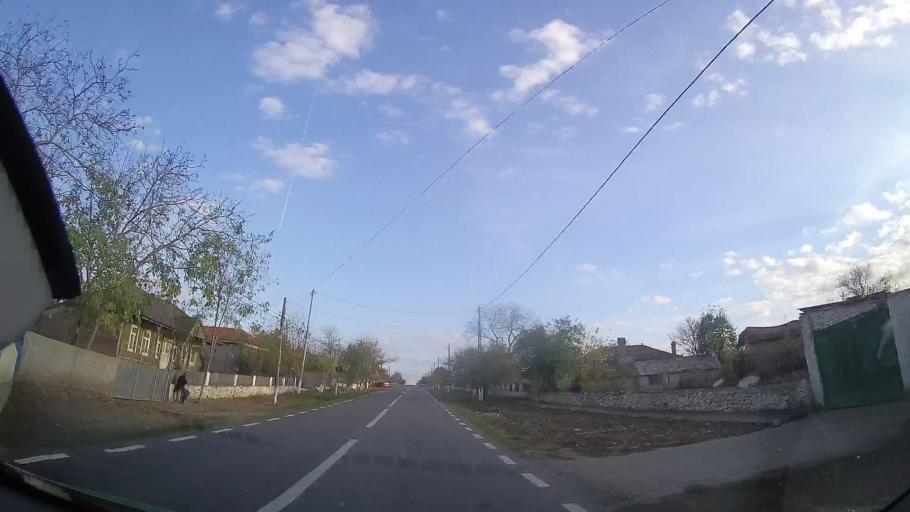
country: RO
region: Constanta
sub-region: Comuna Chirnogeni
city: Plopeni
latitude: 43.9612
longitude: 28.1427
